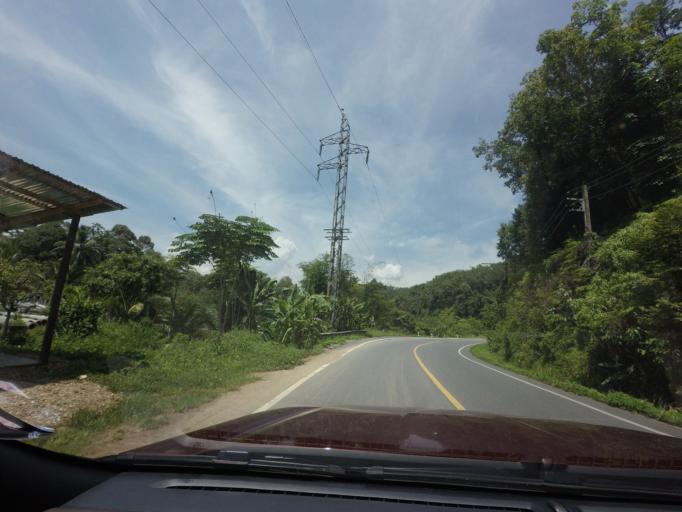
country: TH
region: Yala
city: Betong
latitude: 5.9182
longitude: 101.1687
